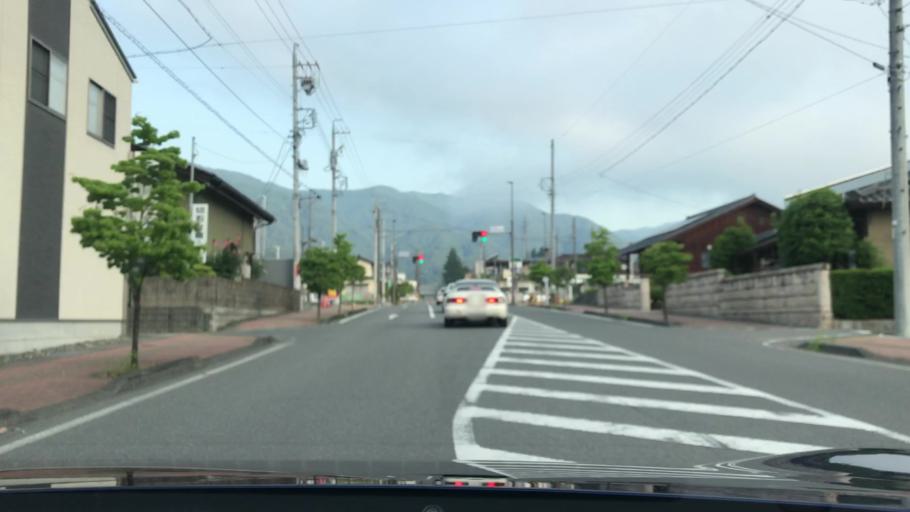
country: JP
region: Nagano
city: Iida
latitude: 35.5113
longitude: 137.8060
